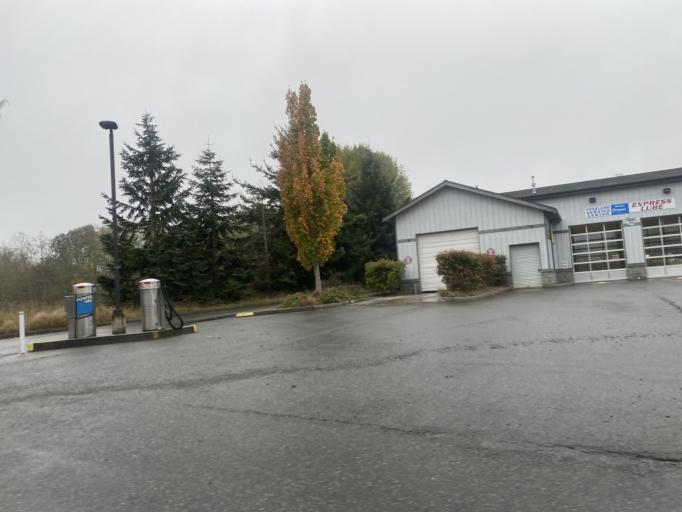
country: US
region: Washington
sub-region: Island County
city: Freeland
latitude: 48.0078
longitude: -122.5317
